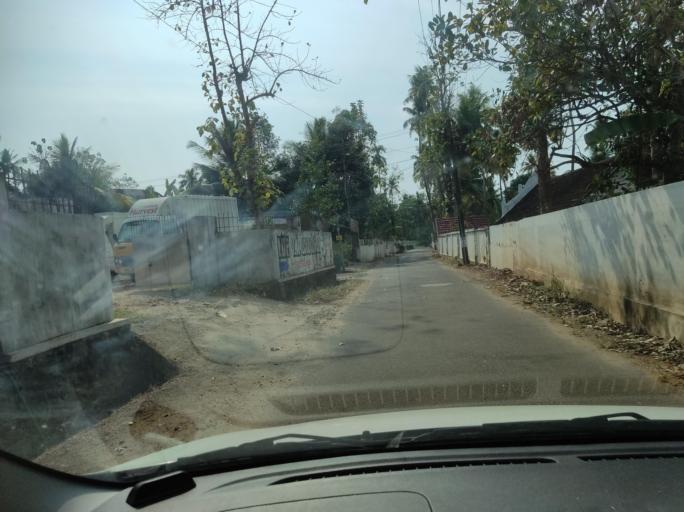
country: IN
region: Kerala
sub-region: Kottayam
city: Kottayam
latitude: 9.6856
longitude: 76.5015
